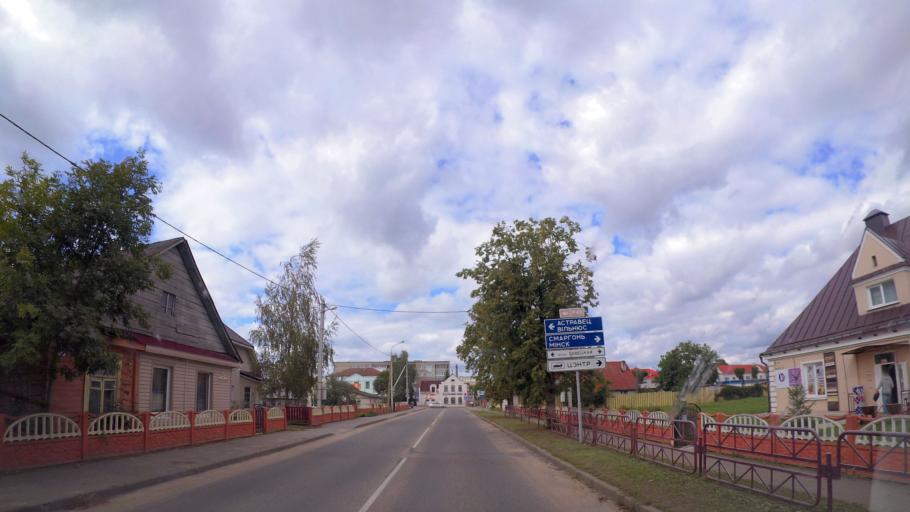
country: BY
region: Grodnenskaya
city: Ashmyany
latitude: 54.4227
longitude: 25.9323
